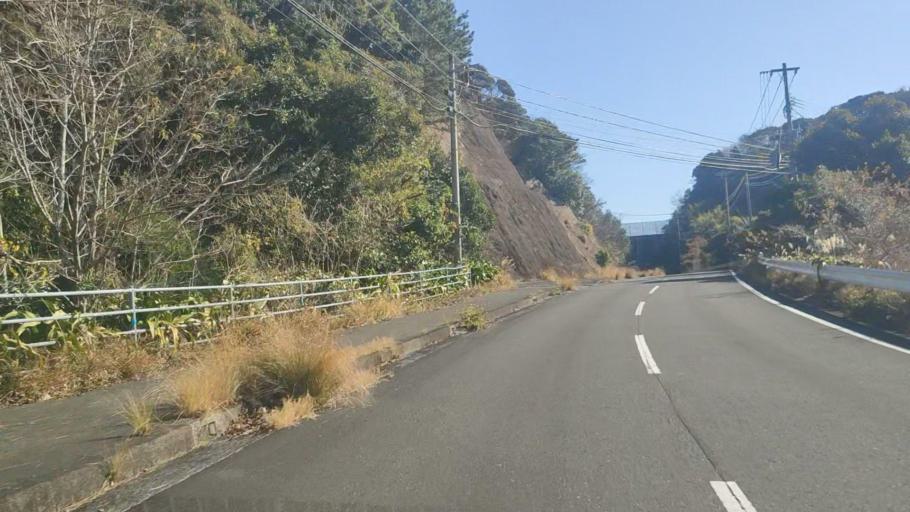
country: JP
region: Oita
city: Saiki
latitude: 32.7951
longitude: 131.9002
